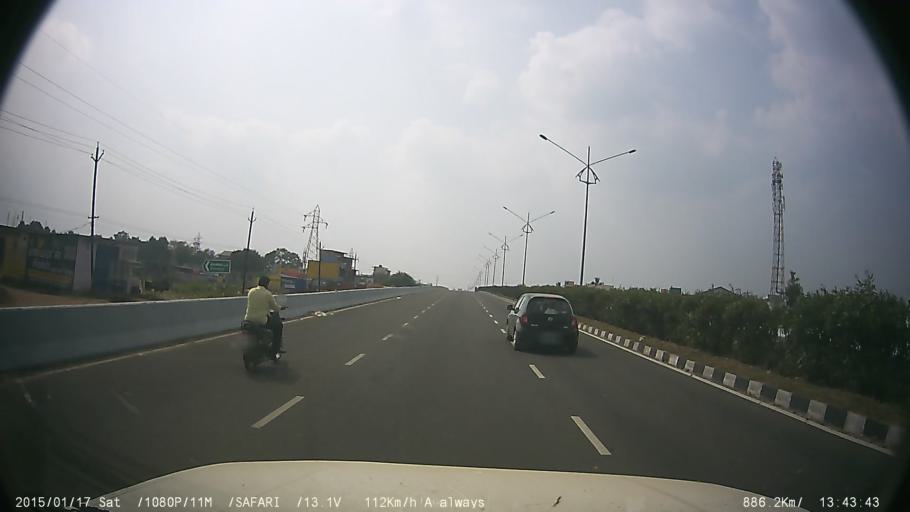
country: IN
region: Tamil Nadu
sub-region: Vellore
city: Vellore
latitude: 12.9259
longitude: 79.1193
